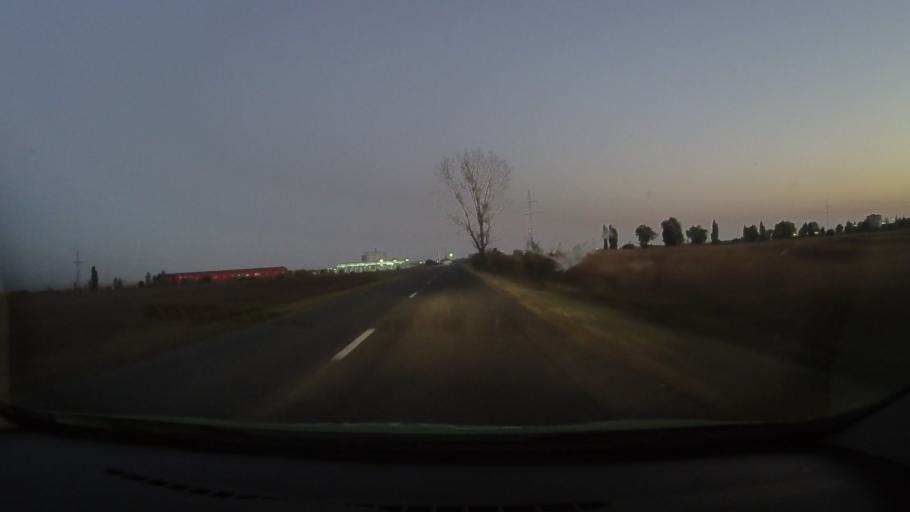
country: RO
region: Arad
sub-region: Comuna Vladimirescu
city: Vladimirescu
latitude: 46.1912
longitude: 21.3919
